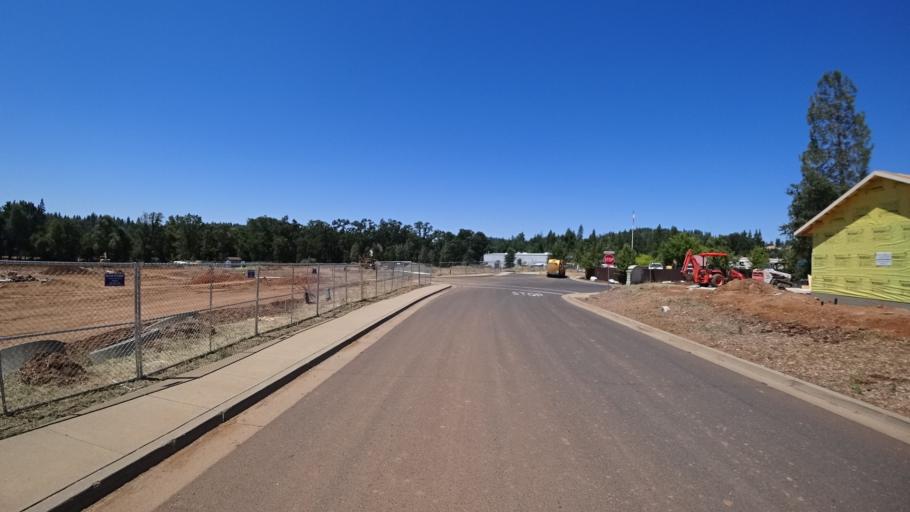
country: US
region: California
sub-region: Calaveras County
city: Murphys
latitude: 38.1404
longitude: -120.4588
